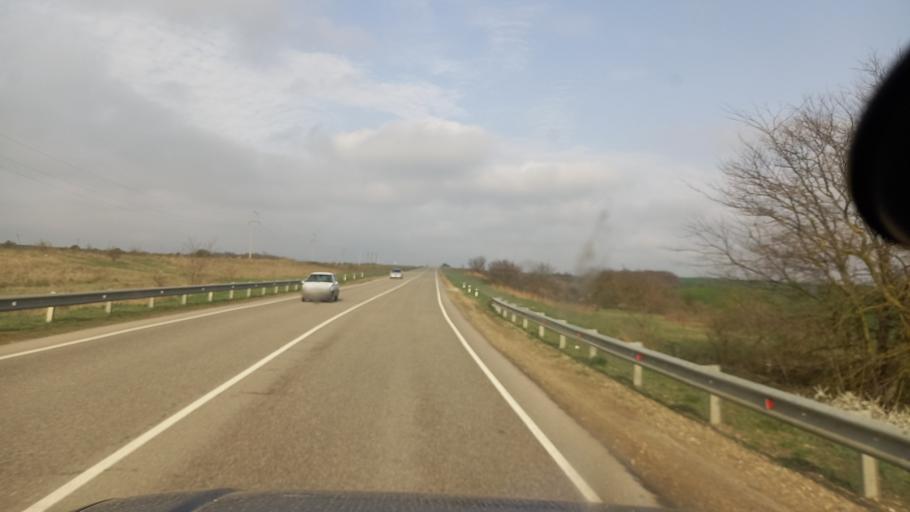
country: RU
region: Krasnodarskiy
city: Varenikovskaya
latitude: 45.0973
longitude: 37.5876
